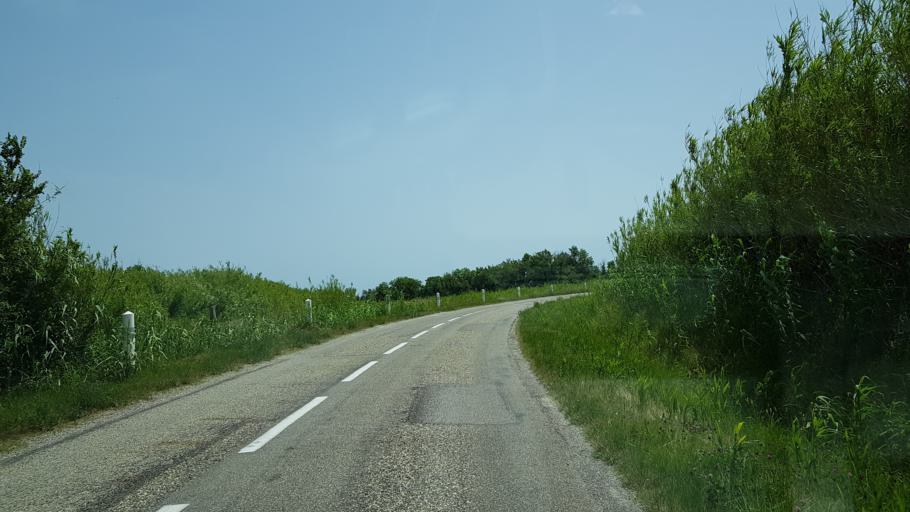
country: FR
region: Provence-Alpes-Cote d'Azur
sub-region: Departement des Bouches-du-Rhone
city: Port-Saint-Louis-du-Rhone
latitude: 43.4398
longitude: 4.6810
